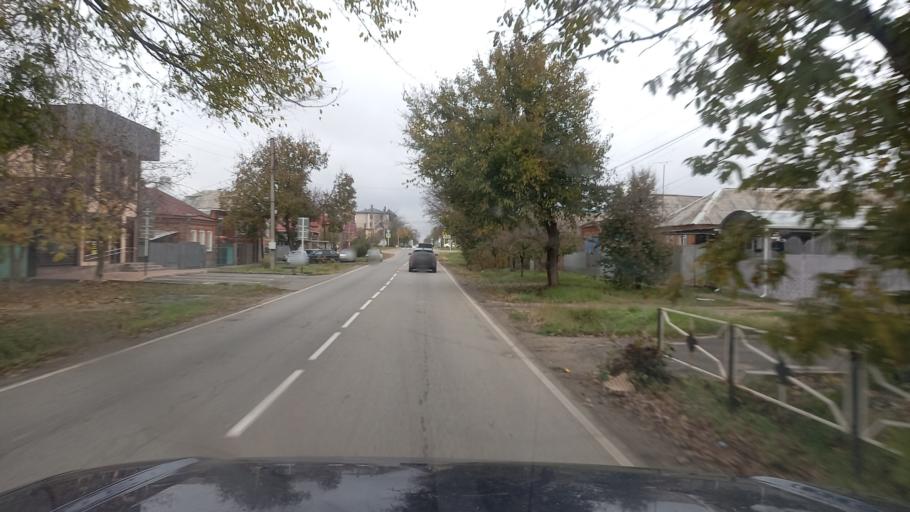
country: RU
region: Adygeya
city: Maykop
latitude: 44.6049
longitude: 40.0713
